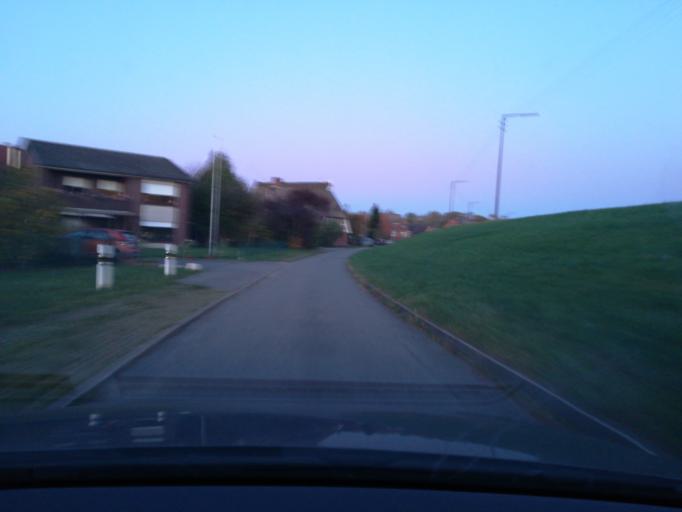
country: DE
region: Lower Saxony
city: Winsen
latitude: 53.4033
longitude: 10.1930
